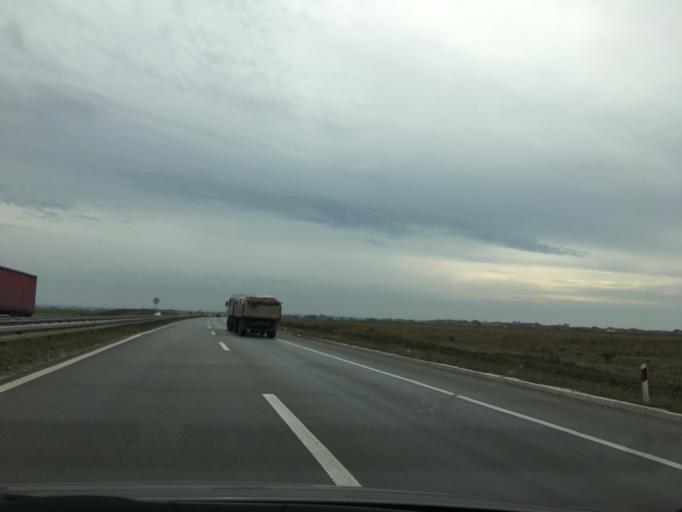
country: RS
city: Novi Banovci
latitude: 44.9146
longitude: 20.3054
